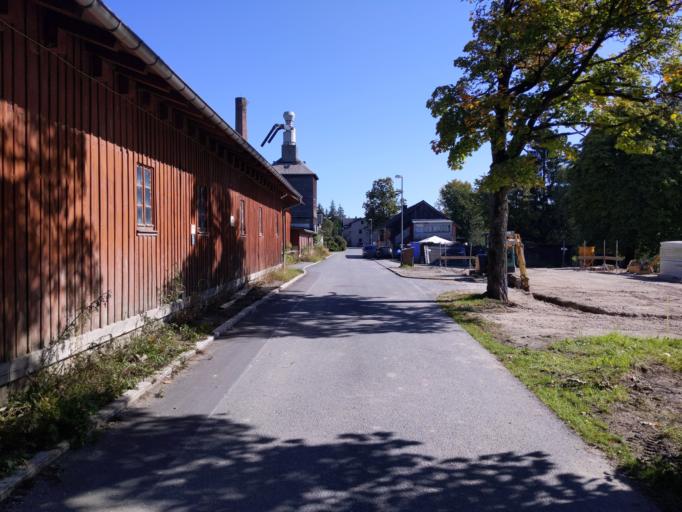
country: DE
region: Saxony
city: Pohl
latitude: 50.3980
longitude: 12.3503
